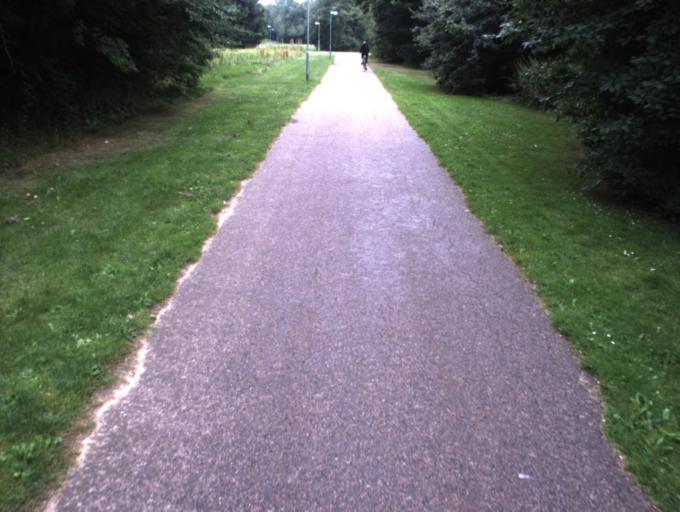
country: SE
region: Skane
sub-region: Helsingborg
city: Helsingborg
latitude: 56.0510
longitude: 12.7402
